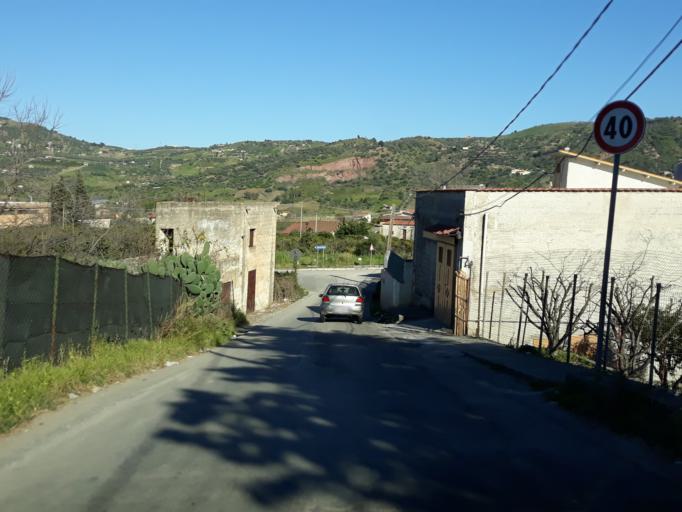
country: IT
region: Sicily
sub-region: Palermo
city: Misilmeri
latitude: 38.0276
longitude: 13.4553
